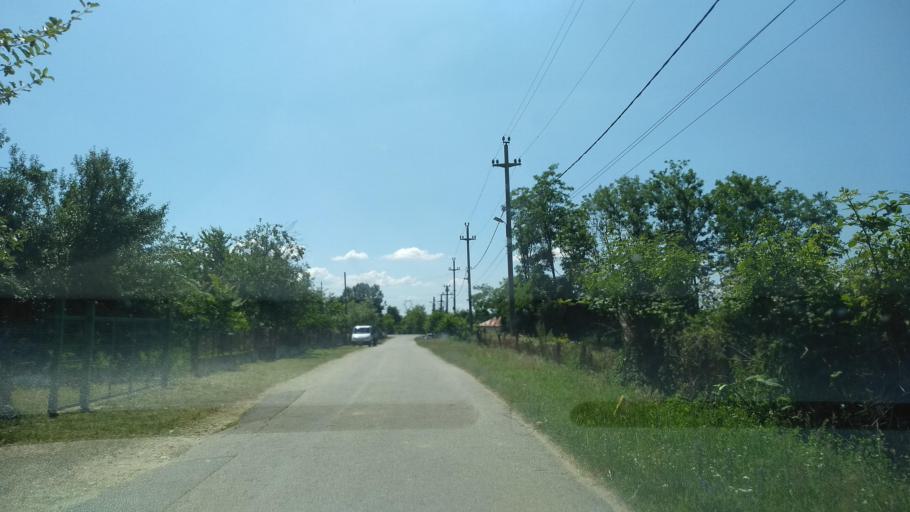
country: RO
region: Gorj
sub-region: Comuna Turcinesti
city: Turcinesti
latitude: 45.1113
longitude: 23.3170
